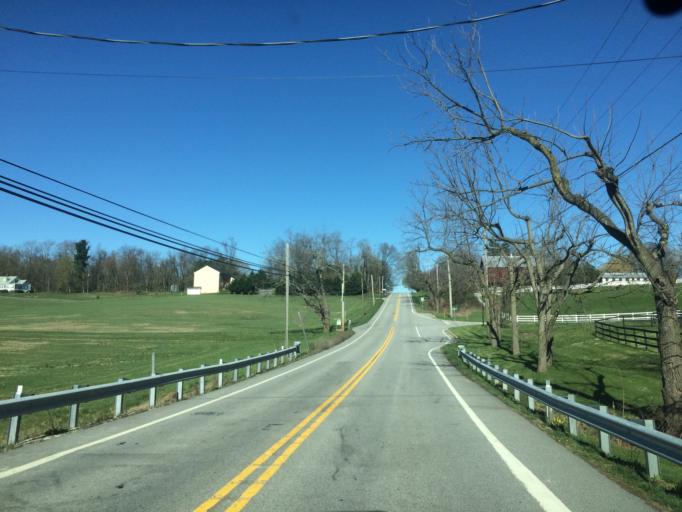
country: US
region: Maryland
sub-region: Carroll County
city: Mount Airy
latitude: 39.3418
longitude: -77.0899
